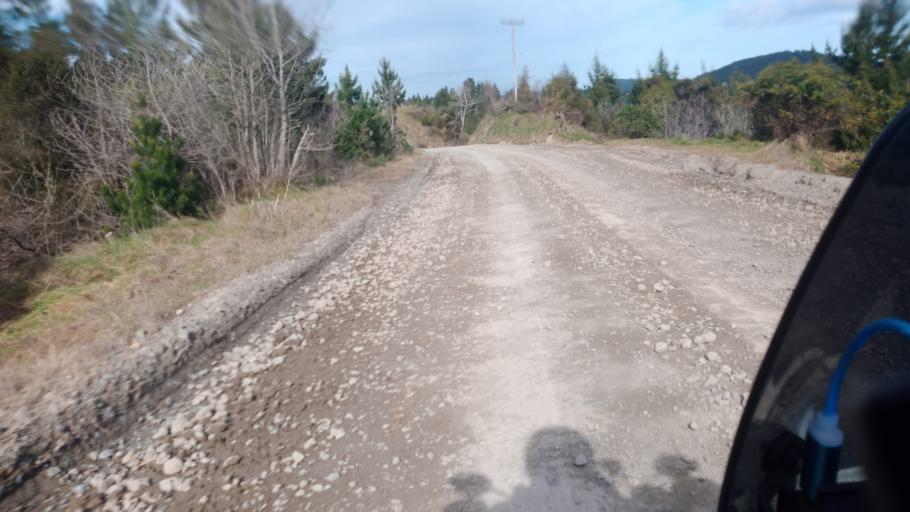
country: NZ
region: Gisborne
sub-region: Gisborne District
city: Gisborne
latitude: -38.1209
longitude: 178.1520
